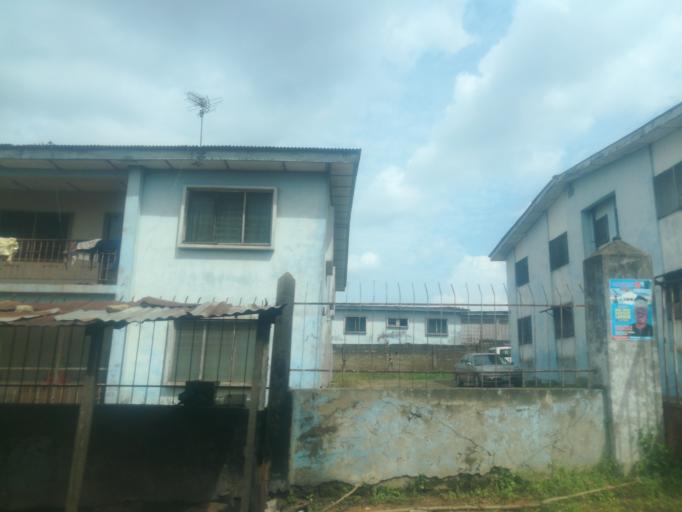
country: NG
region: Oyo
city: Ibadan
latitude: 7.4206
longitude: 3.9313
